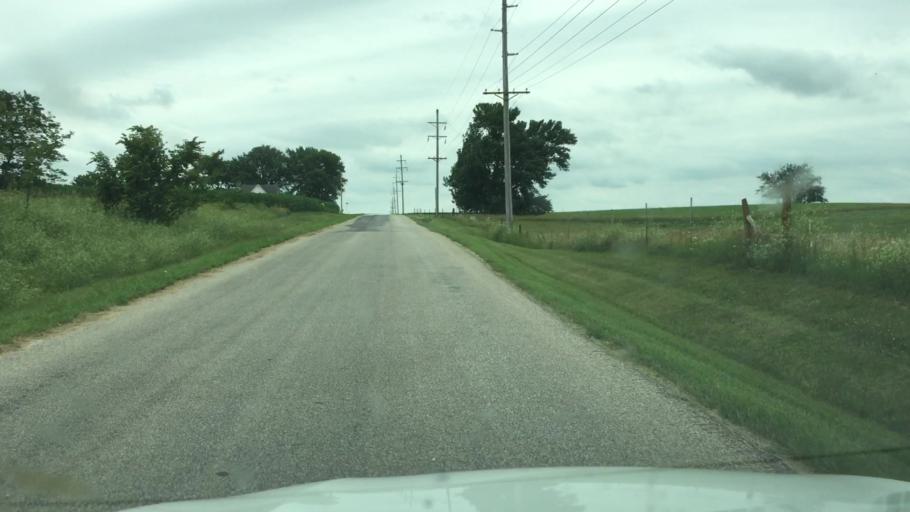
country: US
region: Illinois
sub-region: Hancock County
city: Carthage
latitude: 40.4028
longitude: -91.0824
